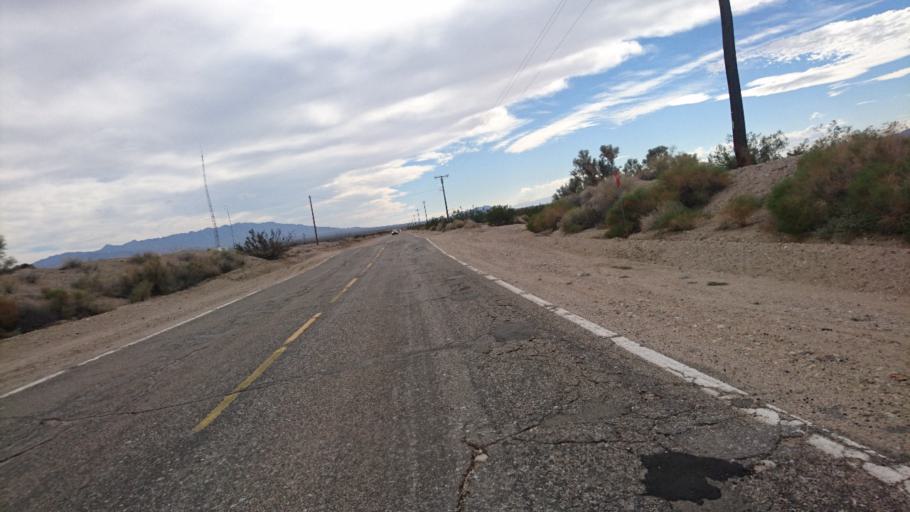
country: US
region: California
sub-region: San Bernardino County
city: Needles
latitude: 34.7695
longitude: -115.2130
